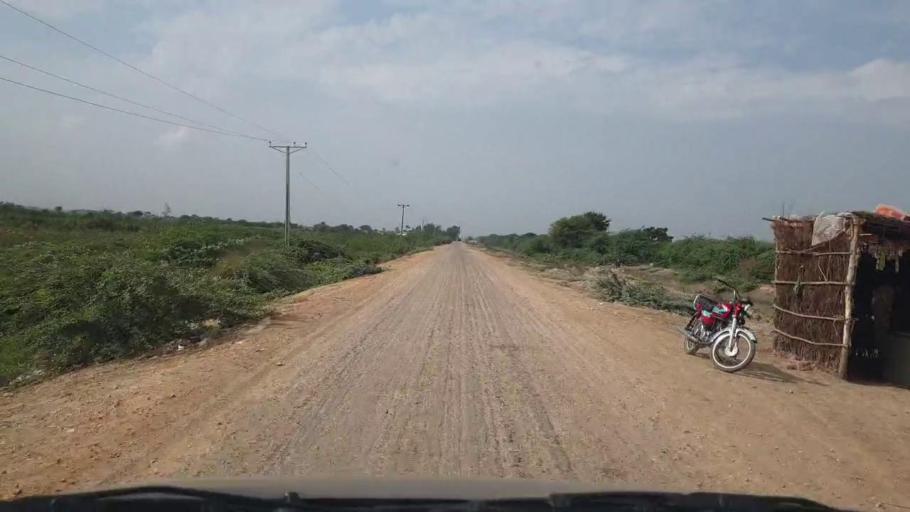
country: PK
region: Sindh
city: Kario
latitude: 24.6277
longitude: 68.5749
